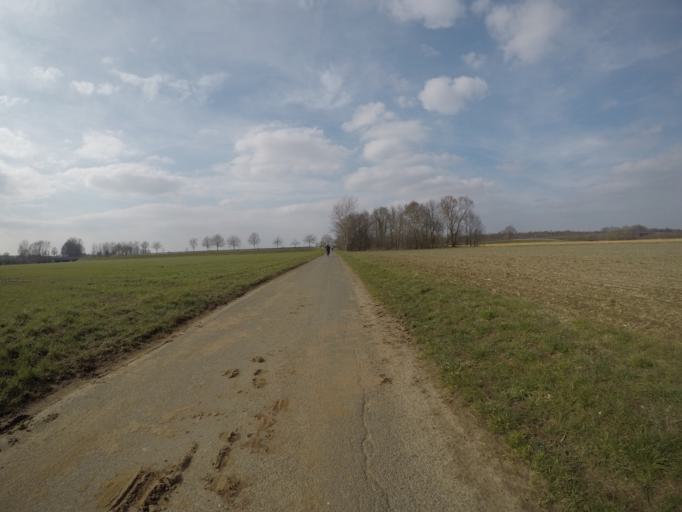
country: DE
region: North Rhine-Westphalia
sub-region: Regierungsbezirk Munster
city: Rhede
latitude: 51.8233
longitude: 6.6809
